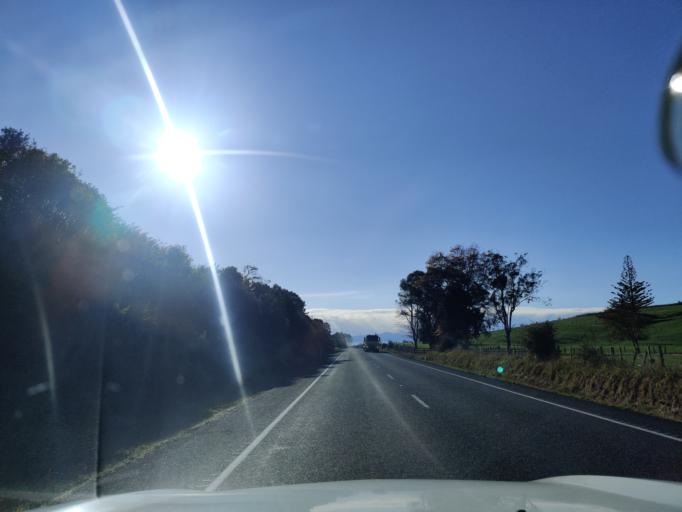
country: NZ
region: Waikato
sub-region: Hauraki District
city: Ngatea
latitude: -37.2842
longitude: 175.3970
